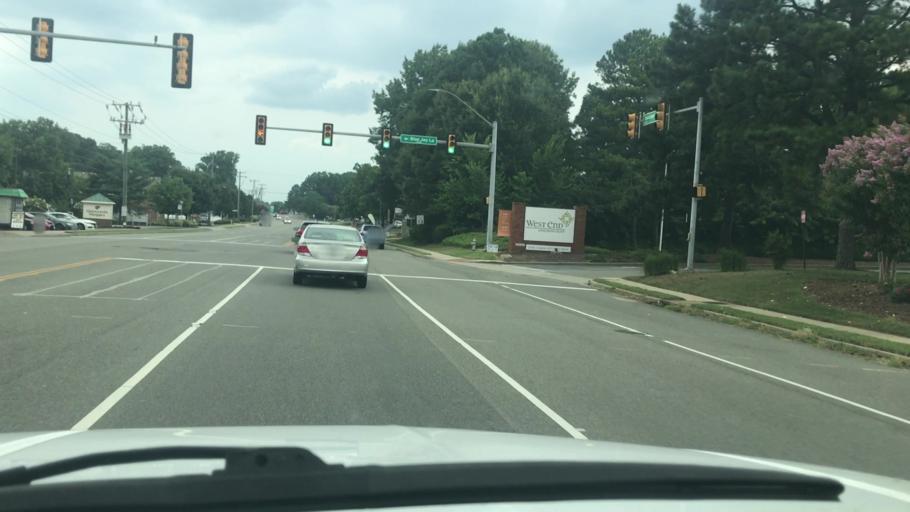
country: US
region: Virginia
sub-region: Henrico County
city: Tuckahoe
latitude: 37.6056
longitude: -77.5719
